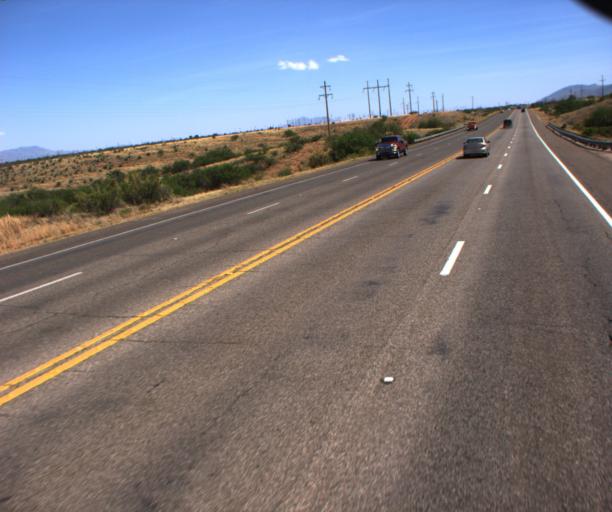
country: US
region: Arizona
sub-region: Cochise County
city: Sierra Vista
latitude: 31.5816
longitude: -110.3188
